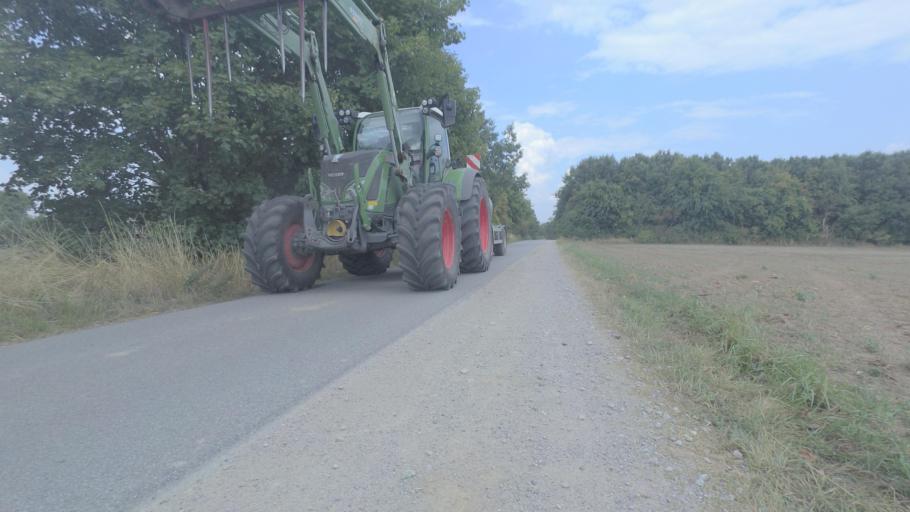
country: DE
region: Mecklenburg-Vorpommern
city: Borrentin
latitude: 53.8278
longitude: 12.9305
